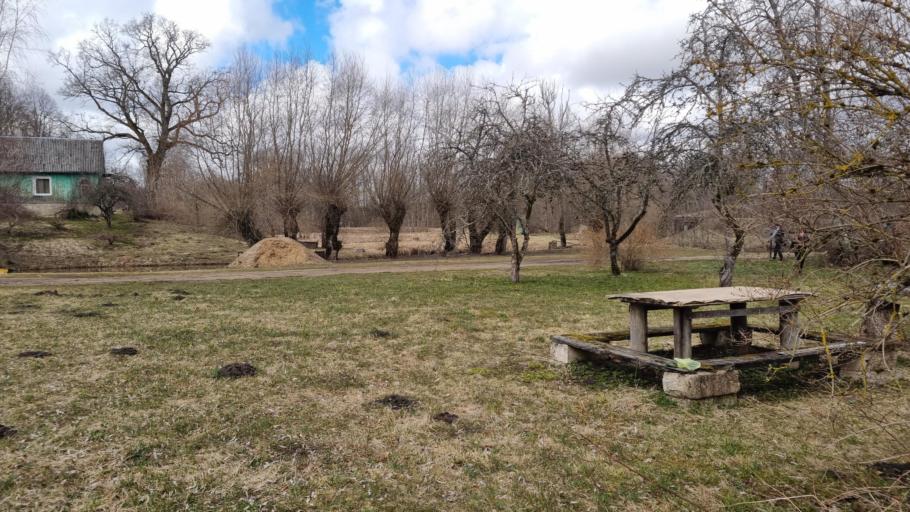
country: LV
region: Vainode
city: Vainode
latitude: 56.3983
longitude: 21.7354
